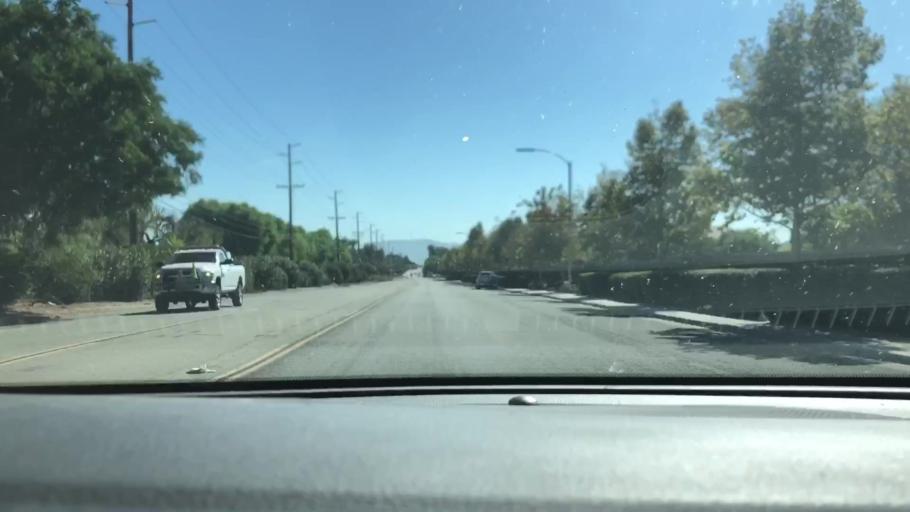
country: US
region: California
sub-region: Riverside County
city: Wildomar
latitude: 33.6011
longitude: -117.2689
